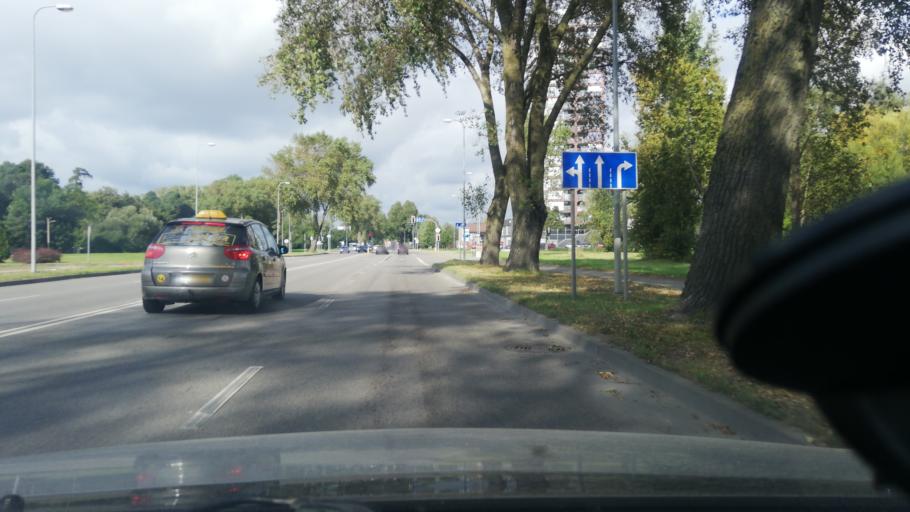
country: LT
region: Klaipedos apskritis
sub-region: Klaipeda
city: Klaipeda
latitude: 55.6696
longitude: 21.1596
